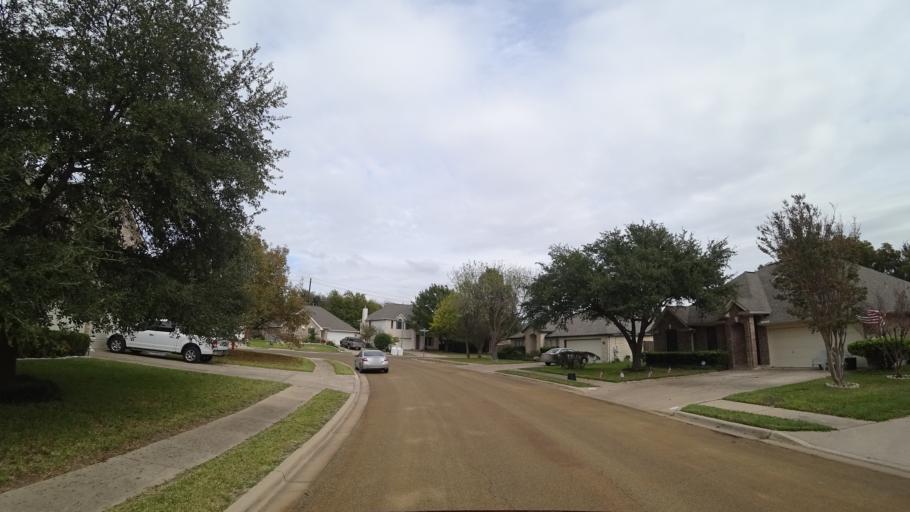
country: US
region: Texas
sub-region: Travis County
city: Wells Branch
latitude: 30.4438
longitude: -97.6720
